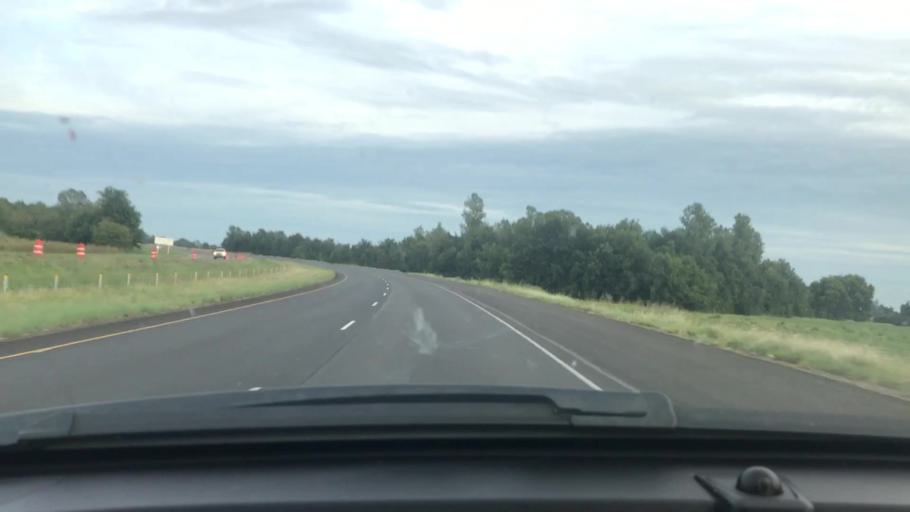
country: US
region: Arkansas
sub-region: Poinsett County
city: Trumann
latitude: 35.6617
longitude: -90.5497
